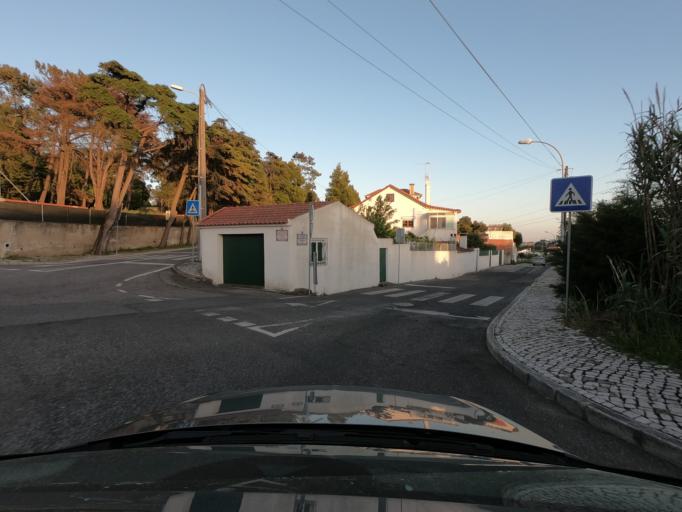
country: PT
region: Lisbon
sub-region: Sintra
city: Rio de Mouro
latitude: 38.7569
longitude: -9.3586
